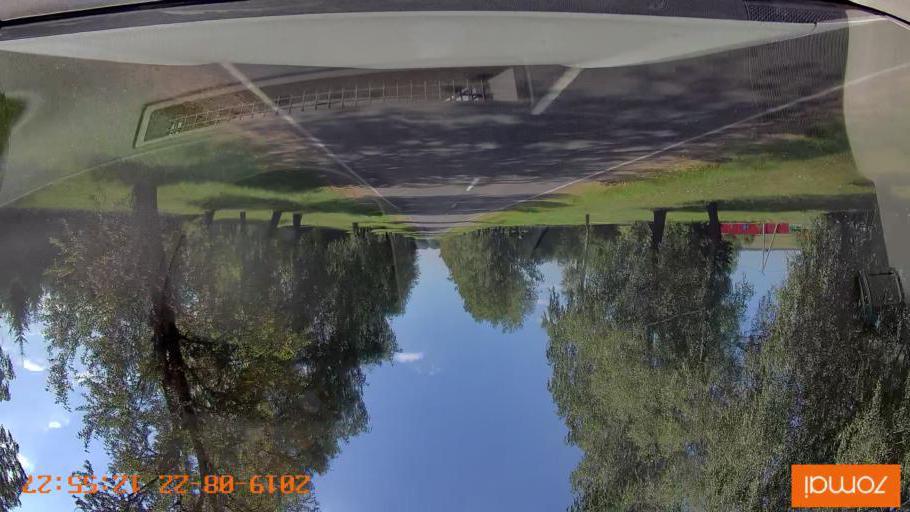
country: BY
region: Minsk
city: Prawdzinski
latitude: 53.4371
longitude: 27.7120
